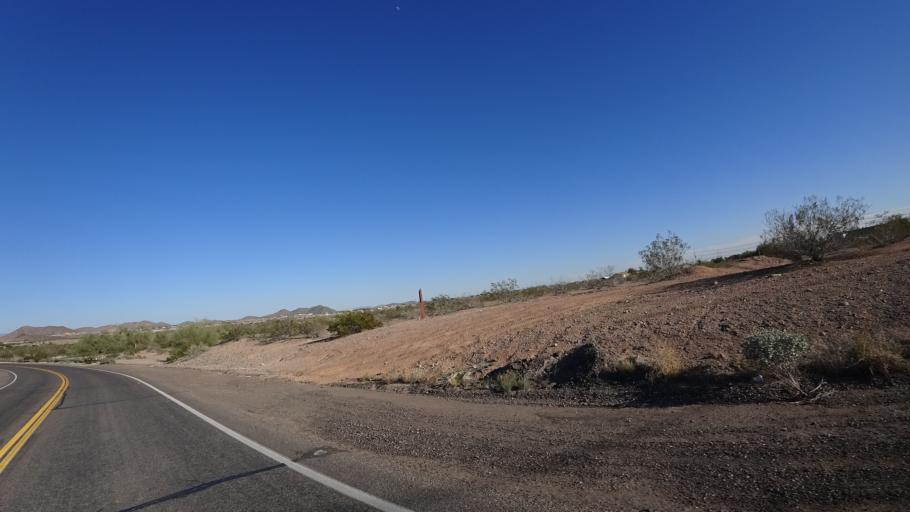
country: US
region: Arizona
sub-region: Maricopa County
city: Sun City West
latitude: 33.7111
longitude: -112.3079
